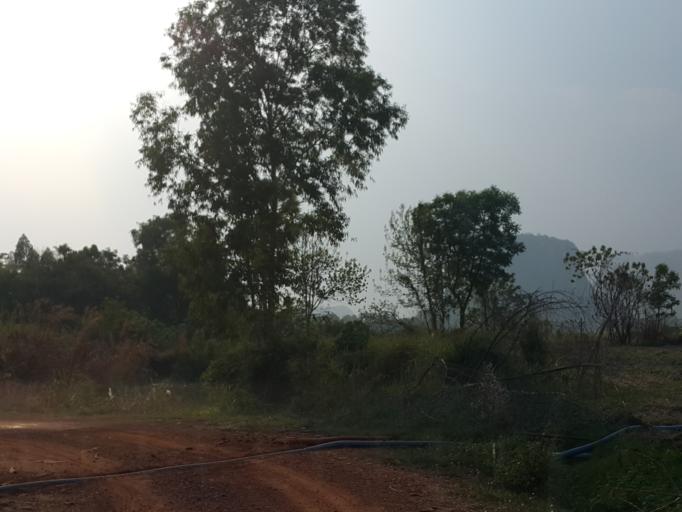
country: TH
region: Uthai Thani
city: Huai Khot
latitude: 15.3199
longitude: 99.6744
